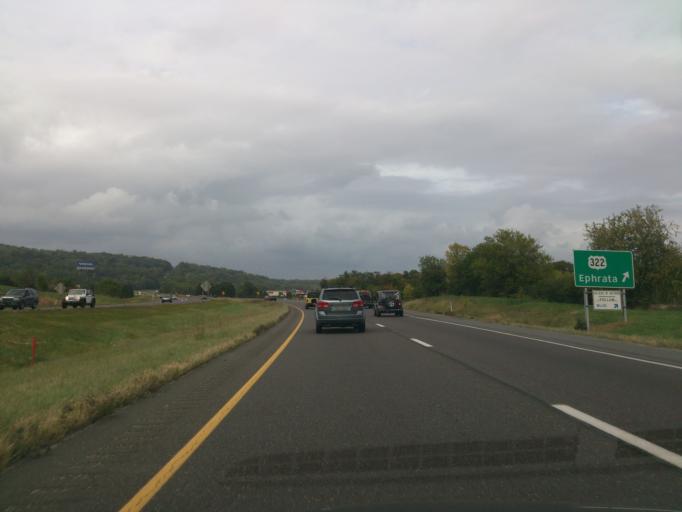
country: US
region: Pennsylvania
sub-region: Lancaster County
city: Ephrata
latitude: 40.1581
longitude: -76.1532
